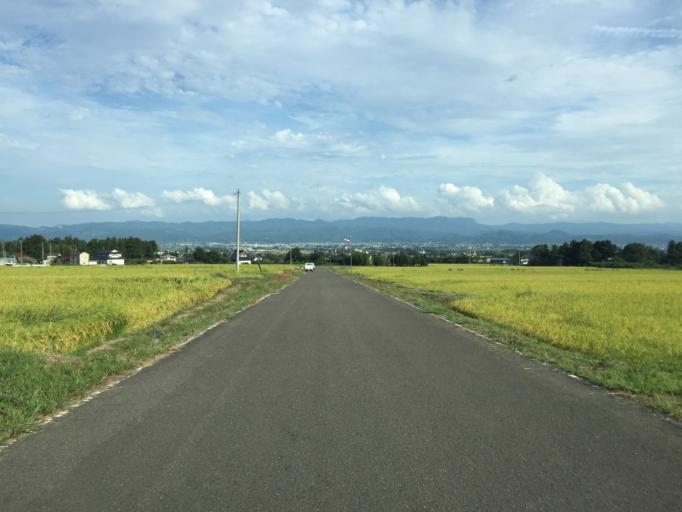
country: JP
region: Fukushima
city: Hobaramachi
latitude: 37.8810
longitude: 140.5214
